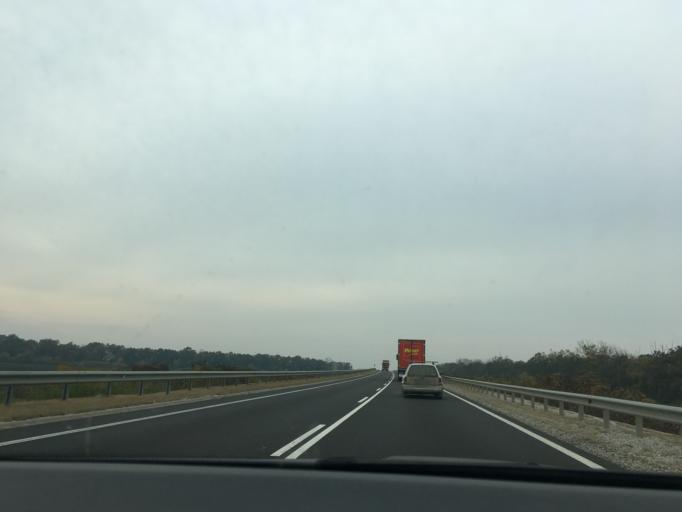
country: HU
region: Jasz-Nagykun-Szolnok
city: Kenderes
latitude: 47.2440
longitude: 20.7165
